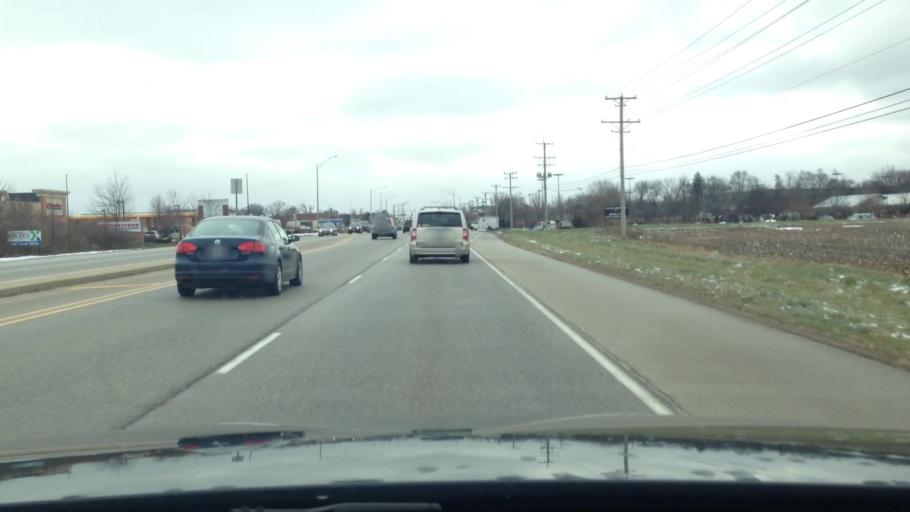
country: US
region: Illinois
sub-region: Kane County
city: Gilberts
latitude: 42.1298
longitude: -88.3356
